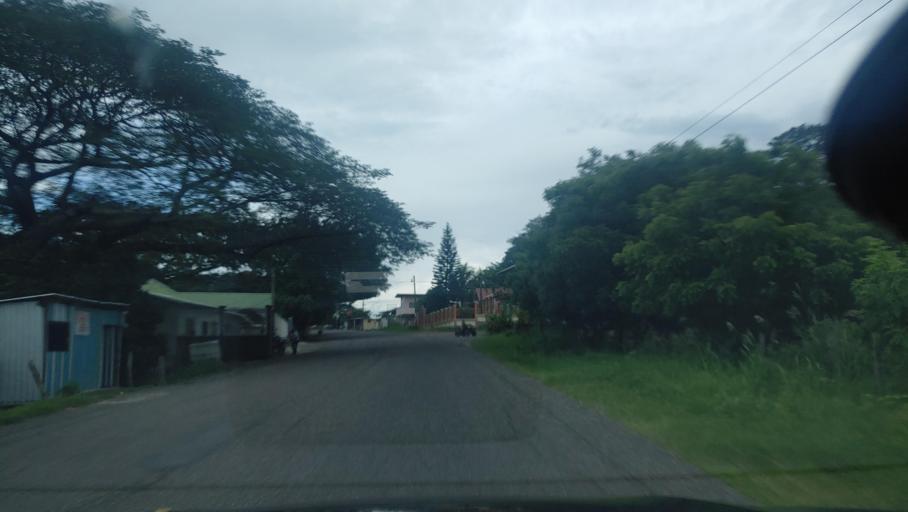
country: HN
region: Choluteca
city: Corpus
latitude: 13.3614
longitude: -86.9897
